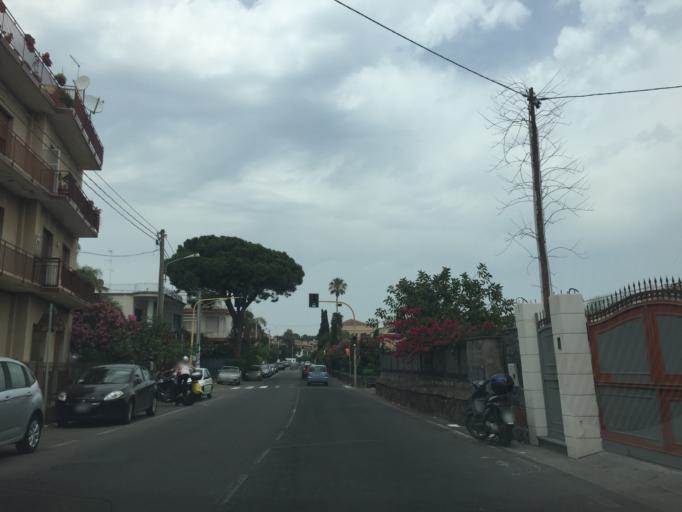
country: IT
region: Sicily
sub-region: Catania
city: Vambolieri
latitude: 37.5698
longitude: 15.1643
